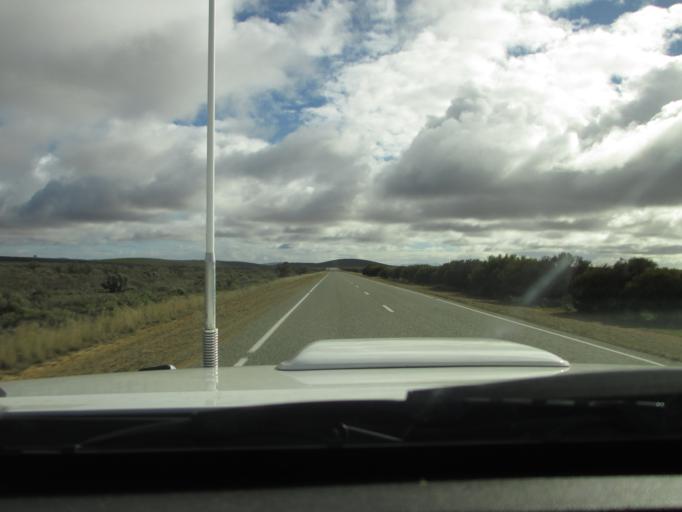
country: AU
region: South Australia
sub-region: Flinders Ranges
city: Quorn
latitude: -32.1736
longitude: 138.5369
